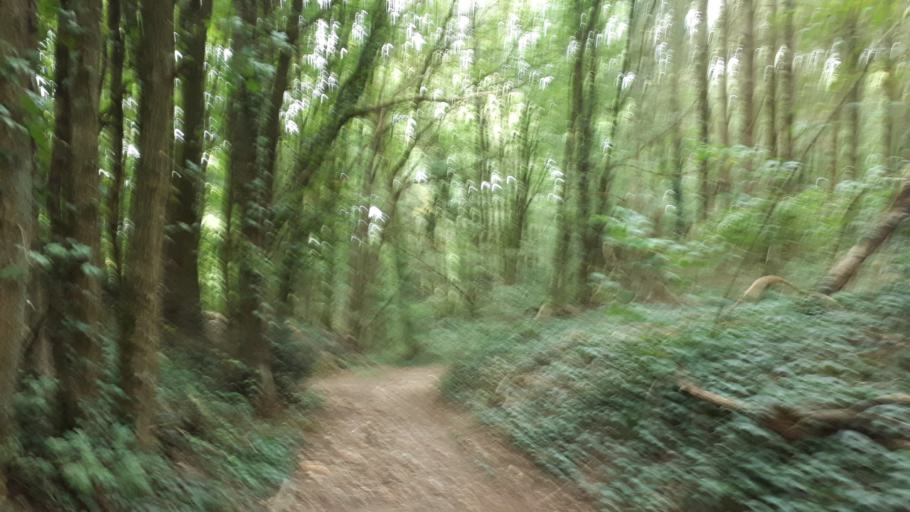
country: FR
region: Centre
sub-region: Departement du Loir-et-Cher
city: Villiers-sur-Loir
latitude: 47.8209
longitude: 0.9761
